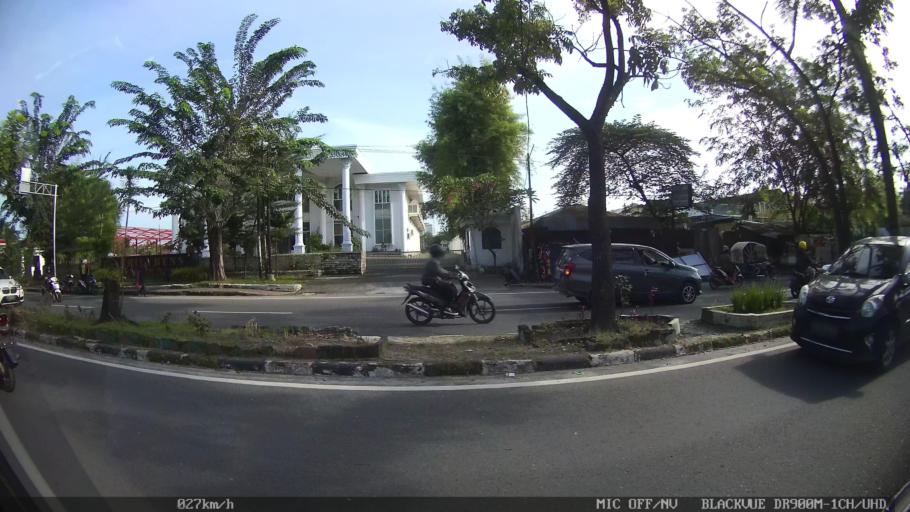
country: ID
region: North Sumatra
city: Medan
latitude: 3.6079
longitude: 98.6528
